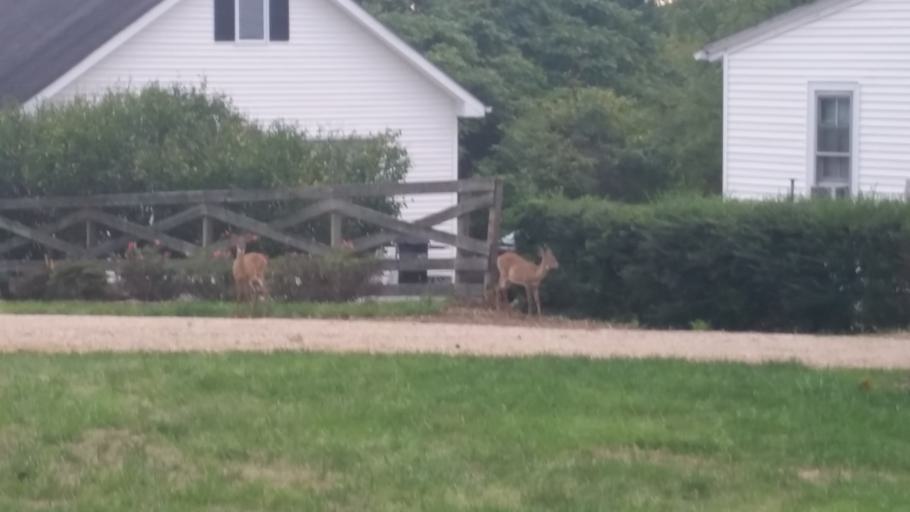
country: US
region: Virginia
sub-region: Franklin County
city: Rocky Mount
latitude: 36.9945
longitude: -79.8865
